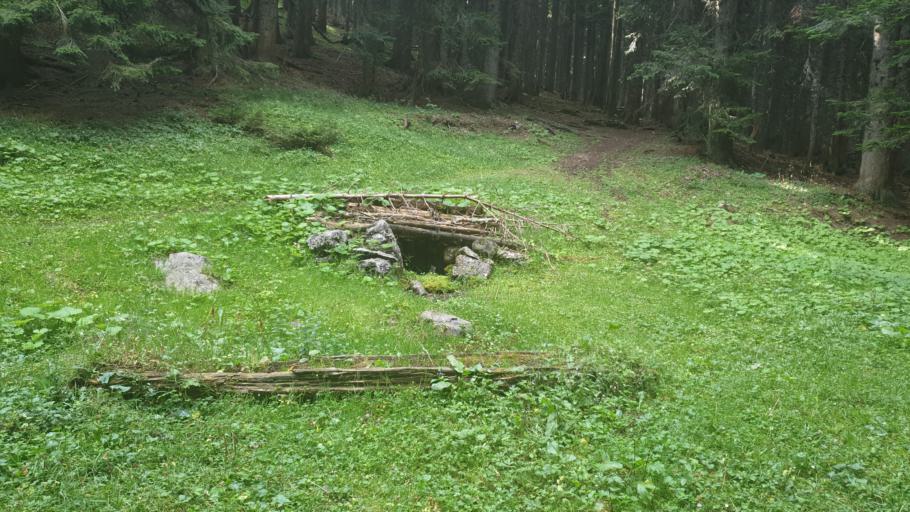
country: ME
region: Opstina Zabljak
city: Zabljak
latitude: 43.1420
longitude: 19.1004
